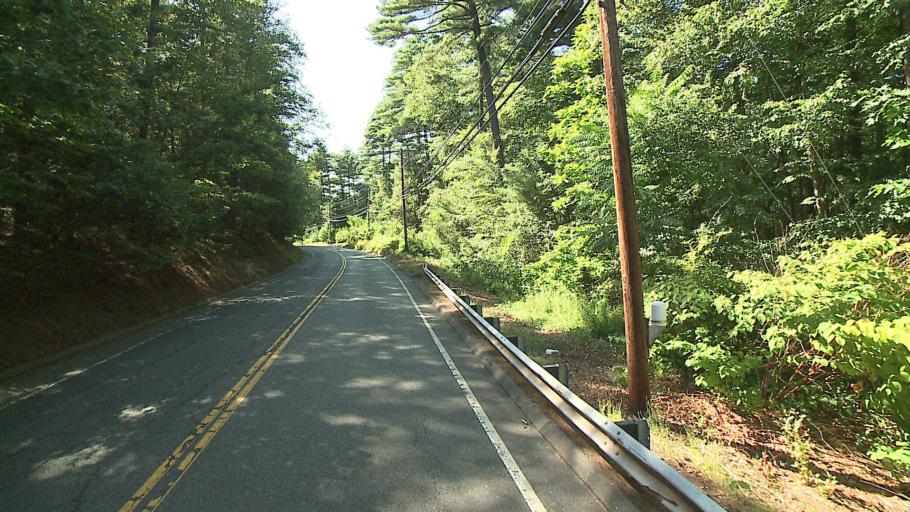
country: US
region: Connecticut
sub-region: Hartford County
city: Simsbury Center
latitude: 41.8692
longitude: -72.8282
